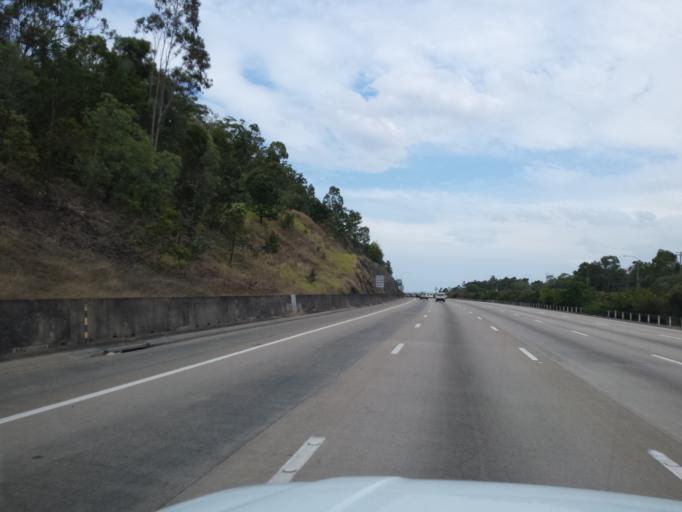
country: AU
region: Queensland
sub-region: Gold Coast
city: Upper Coomera
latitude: -27.9208
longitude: 153.3242
